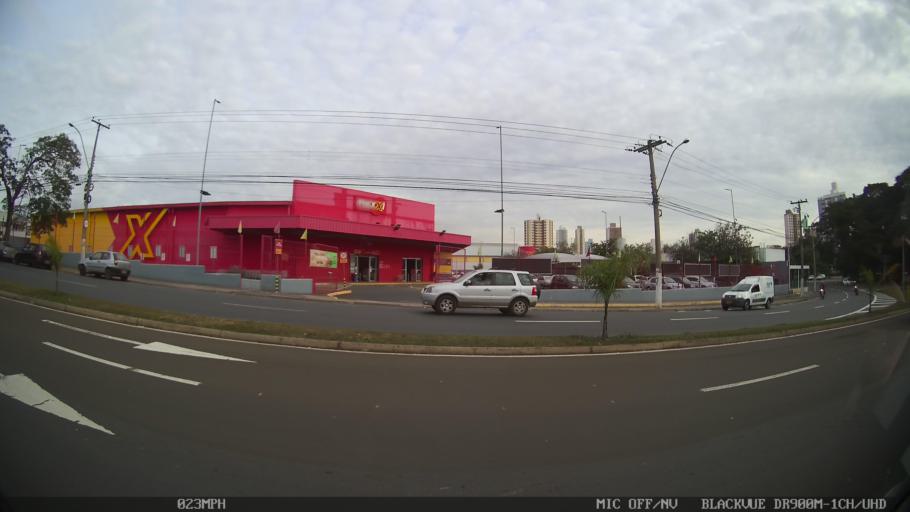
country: BR
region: Sao Paulo
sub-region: Piracicaba
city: Piracicaba
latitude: -22.7258
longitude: -47.6254
